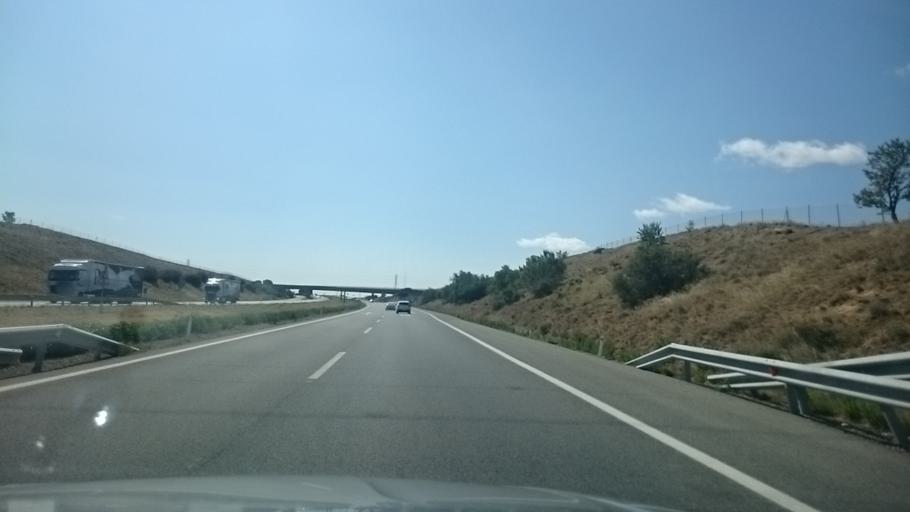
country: ES
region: Aragon
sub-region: Provincia de Zaragoza
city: Mallen
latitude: 41.8548
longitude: -1.3815
